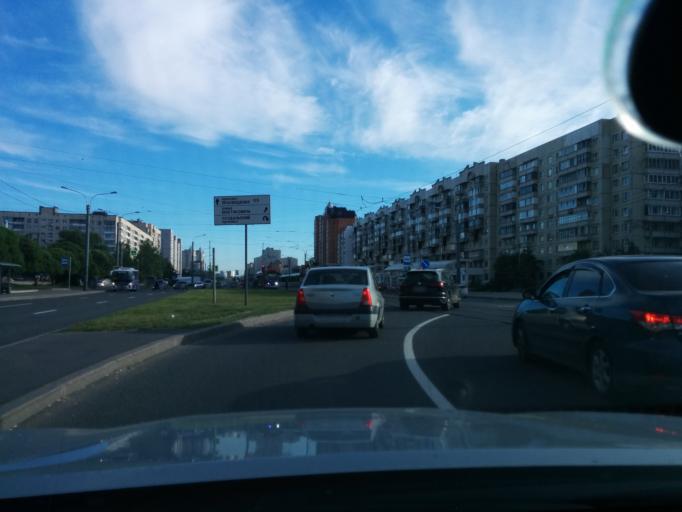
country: RU
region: Leningrad
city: Parnas
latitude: 60.0571
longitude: 30.3382
